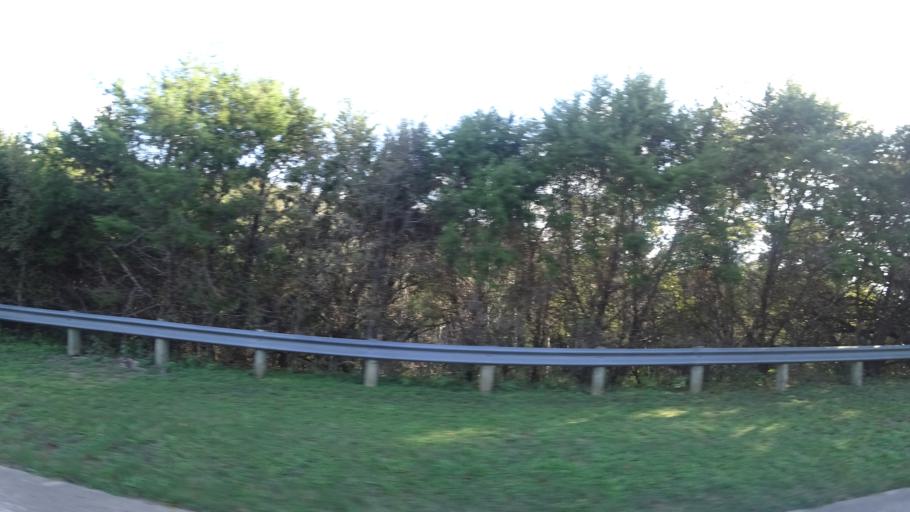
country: US
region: Texas
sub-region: Travis County
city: Barton Creek
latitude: 30.2768
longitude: -97.8682
